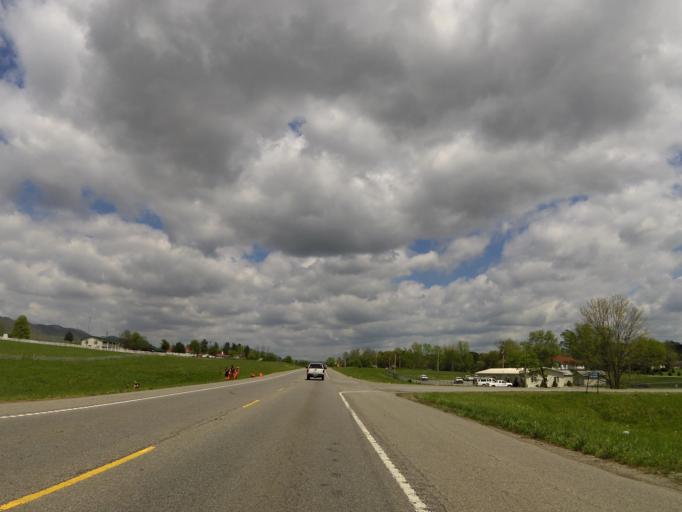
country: US
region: Tennessee
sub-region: Campbell County
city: Fincastle
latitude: 36.4029
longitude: -84.0745
